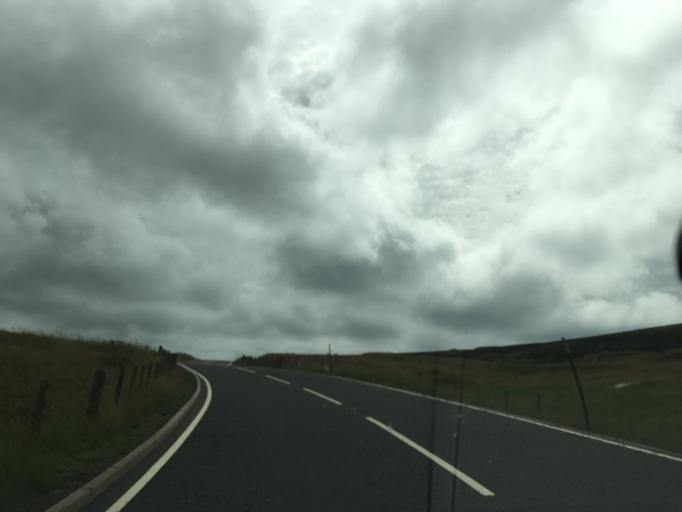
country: GB
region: Scotland
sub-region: Dumfries and Galloway
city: Sanquhar
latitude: 55.4098
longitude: -3.7664
